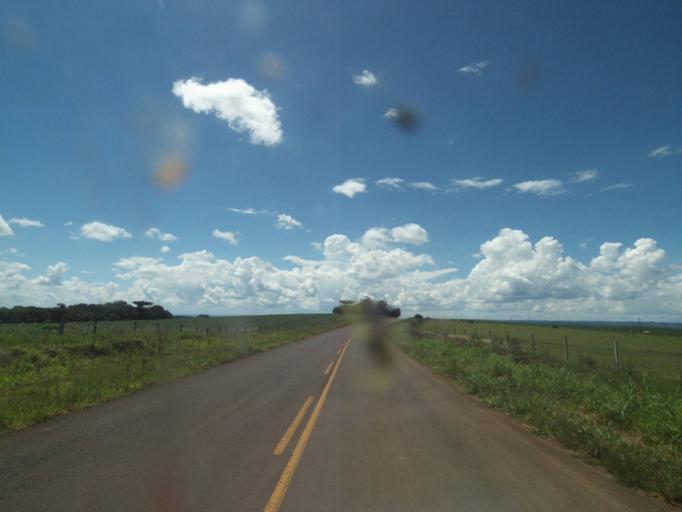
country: BR
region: Parana
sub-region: Pinhao
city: Pinhao
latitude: -25.8063
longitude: -52.0719
